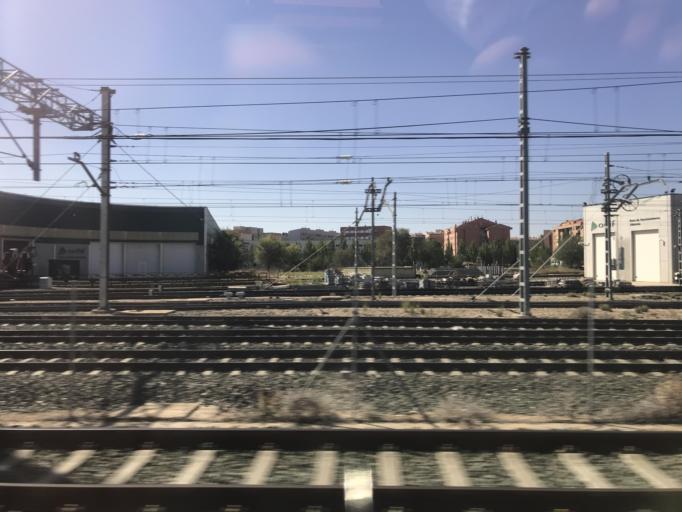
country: ES
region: Castille-La Mancha
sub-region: Provincia de Albacete
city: Albacete
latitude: 39.0044
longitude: -1.8515
